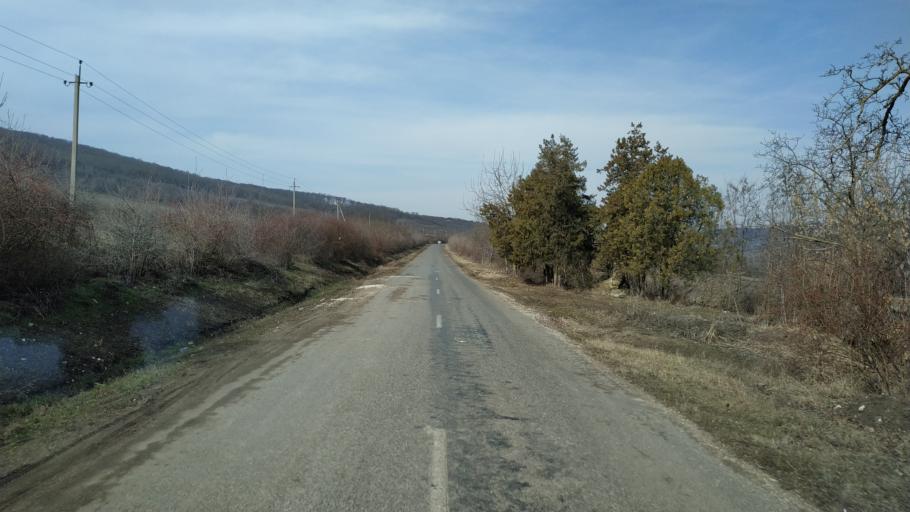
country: MD
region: Nisporeni
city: Nisporeni
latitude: 47.1774
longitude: 28.0840
